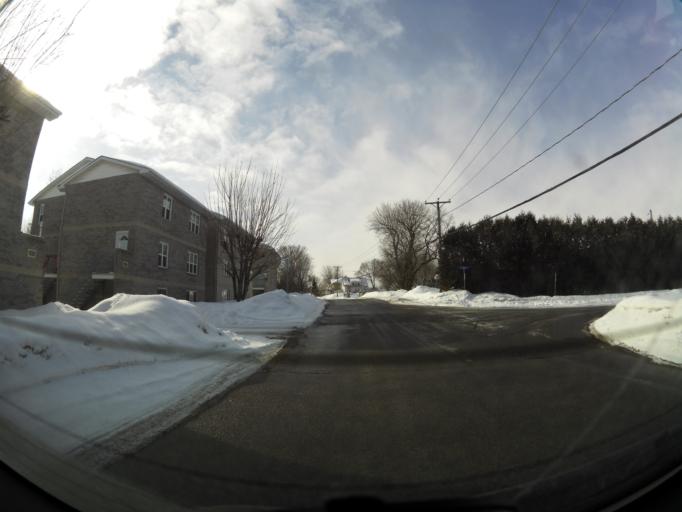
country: CA
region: Quebec
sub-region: Outaouais
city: Gatineau
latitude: 45.4895
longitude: -75.5920
